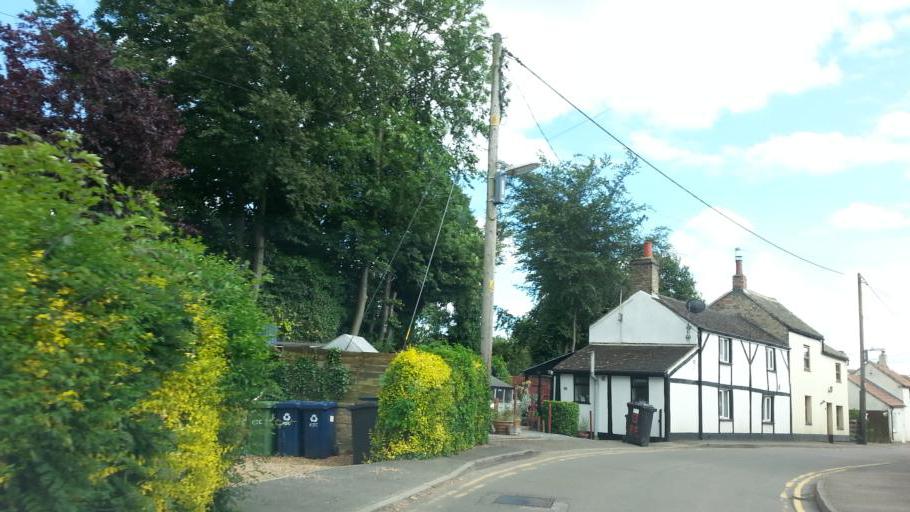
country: GB
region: England
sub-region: Cambridgeshire
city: Earith
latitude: 52.3552
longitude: 0.0364
